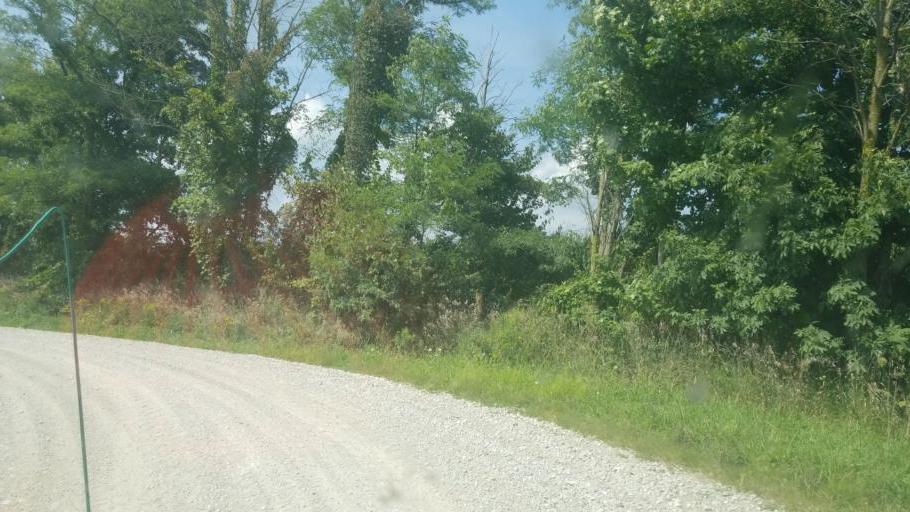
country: US
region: Ohio
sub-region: Huron County
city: New London
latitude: 40.9860
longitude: -82.4083
